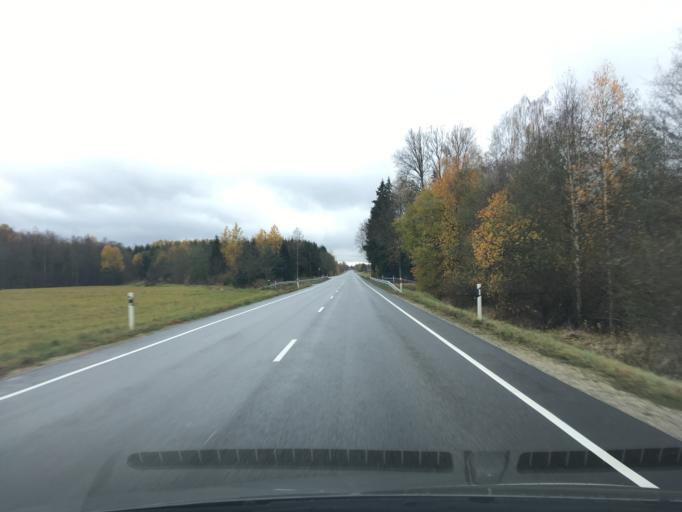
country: EE
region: Jogevamaa
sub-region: Tabivere vald
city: Tabivere
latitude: 58.4431
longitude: 26.5073
